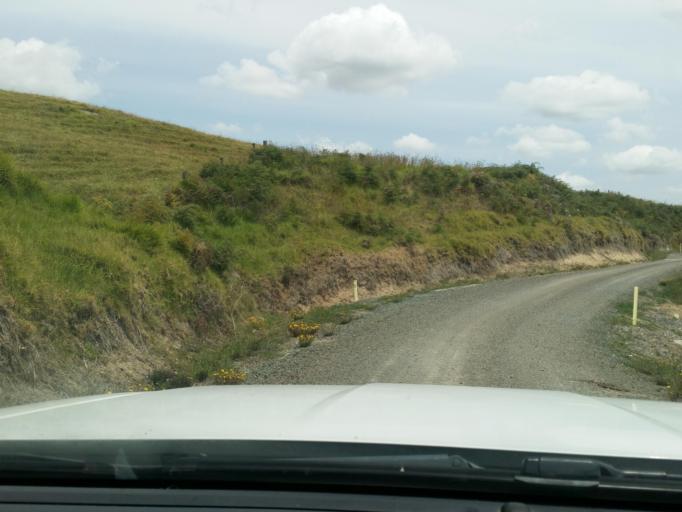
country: NZ
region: Northland
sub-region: Whangarei
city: Maungatapere
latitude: -35.9829
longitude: 174.2236
